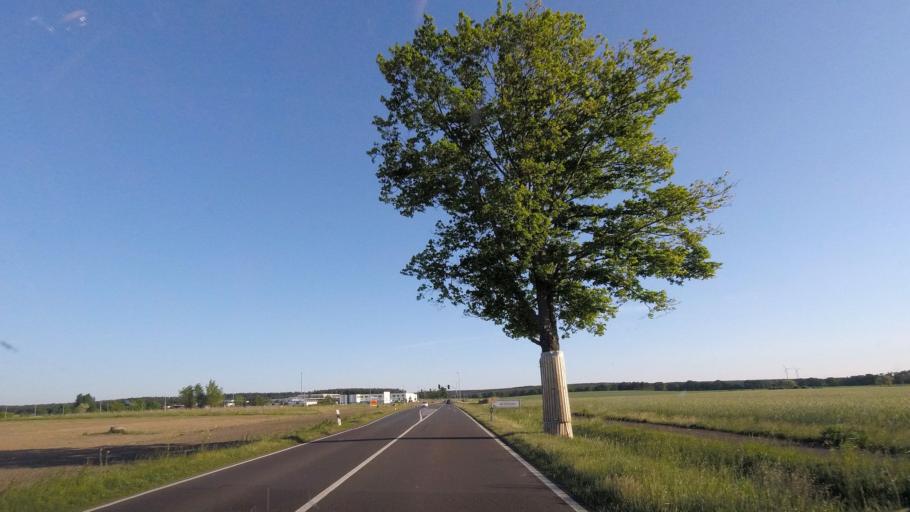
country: DE
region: Brandenburg
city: Brandenburg an der Havel
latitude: 52.3825
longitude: 12.5942
